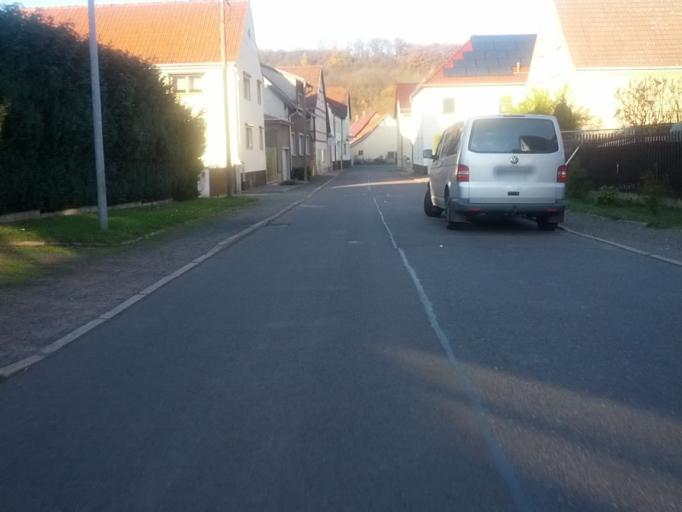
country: DE
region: Thuringia
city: Mechterstadt
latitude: 50.9437
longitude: 10.4786
